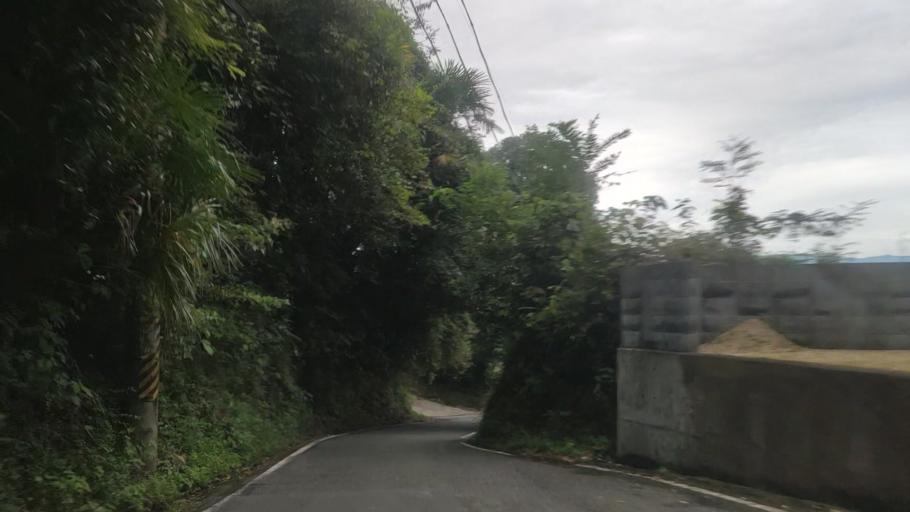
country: JP
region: Wakayama
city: Hashimoto
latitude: 34.3105
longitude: 135.6231
